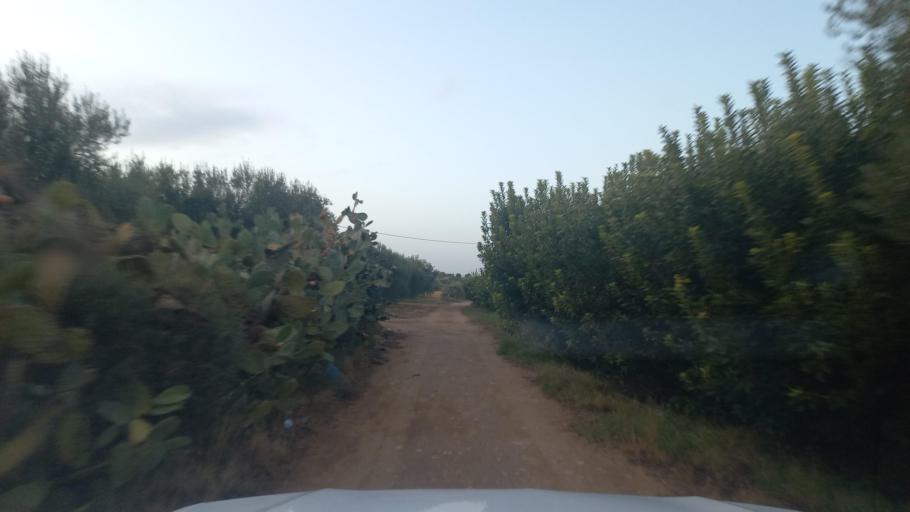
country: TN
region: Al Qasrayn
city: Kasserine
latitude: 35.2226
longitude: 9.0513
